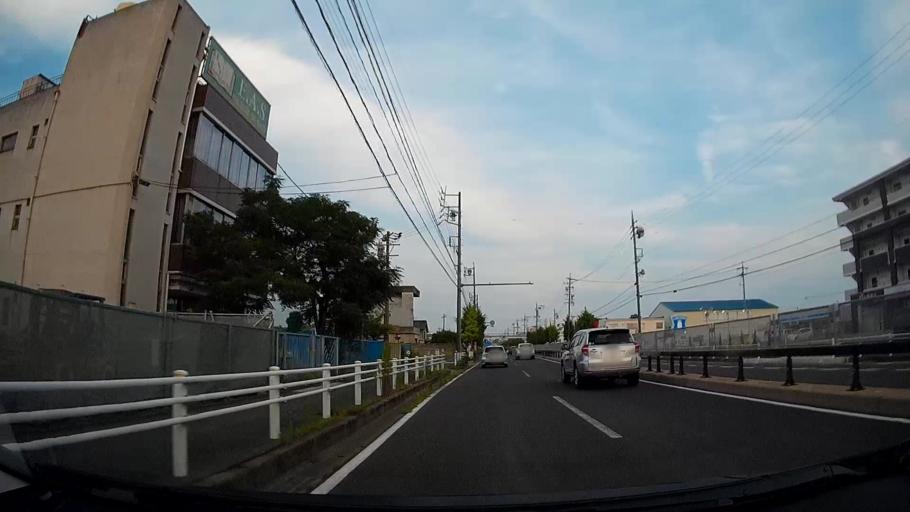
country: JP
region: Aichi
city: Toyohashi
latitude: 34.7812
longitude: 137.3824
